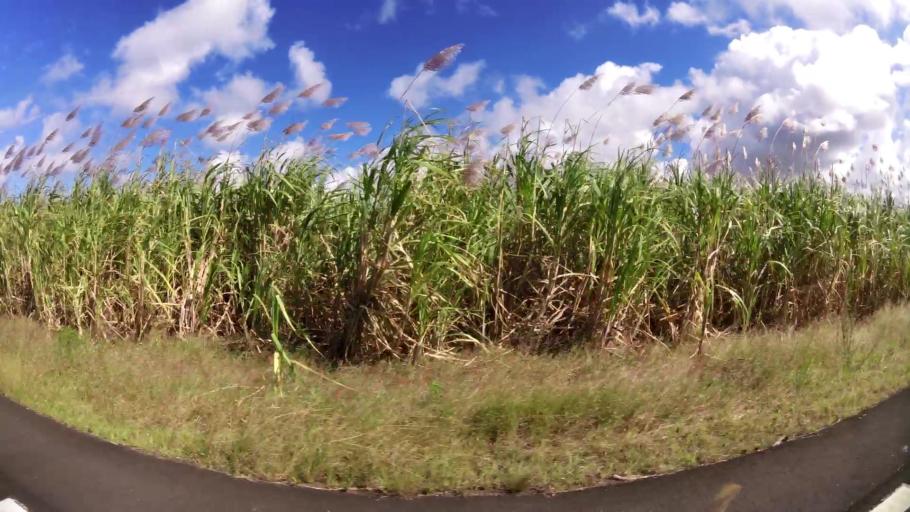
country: MU
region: Grand Port
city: Beau Vallon
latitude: -20.4251
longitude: 57.6995
